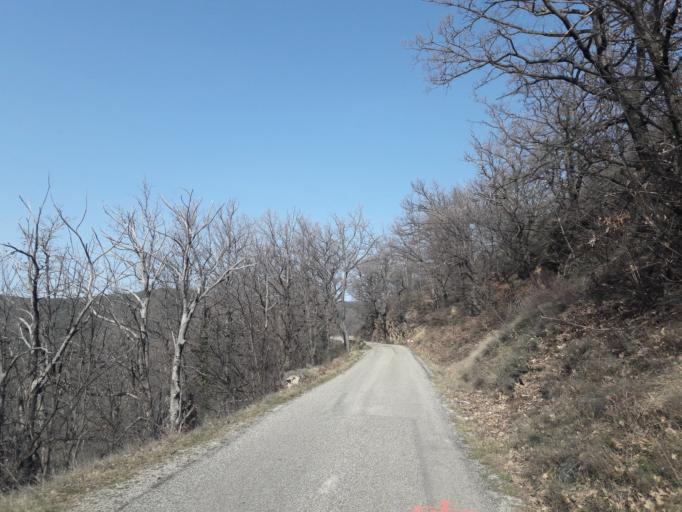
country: FR
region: Languedoc-Roussillon
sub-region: Departement du Gard
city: Sumene
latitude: 43.9951
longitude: 3.7645
